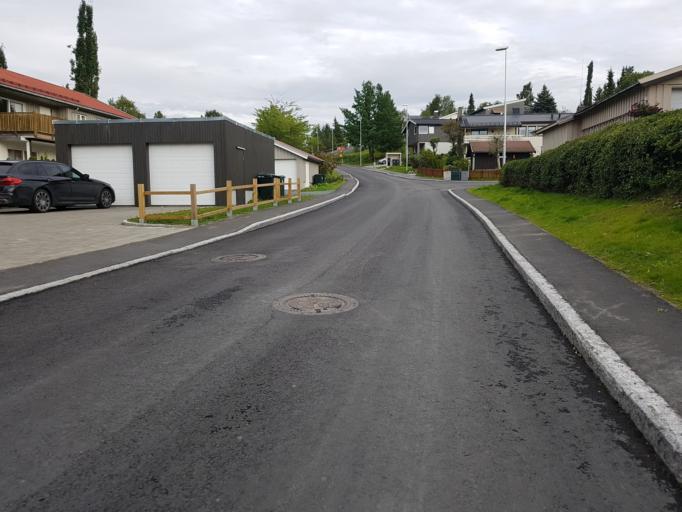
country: NO
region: Sor-Trondelag
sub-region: Trondheim
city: Trondheim
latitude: 63.4017
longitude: 10.4149
